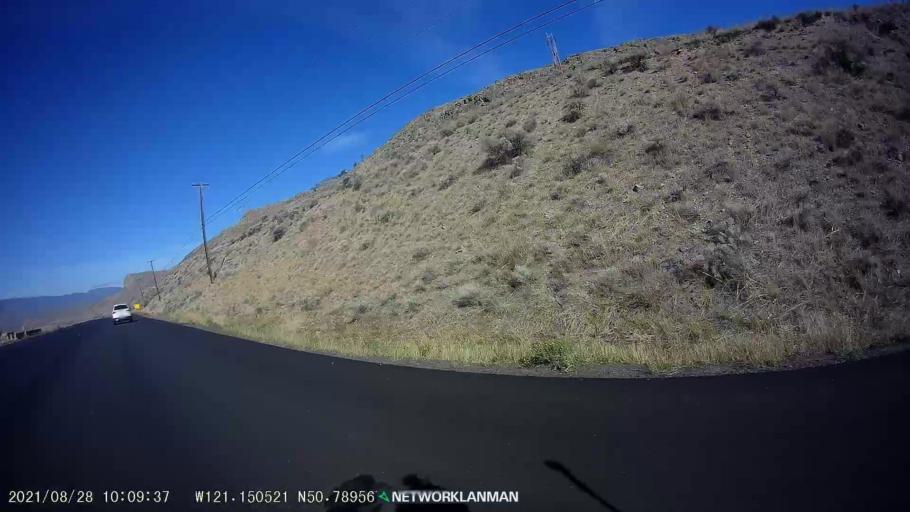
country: CA
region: British Columbia
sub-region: Thompson-Nicola Regional District
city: Ashcroft
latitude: 50.7896
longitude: -121.1510
